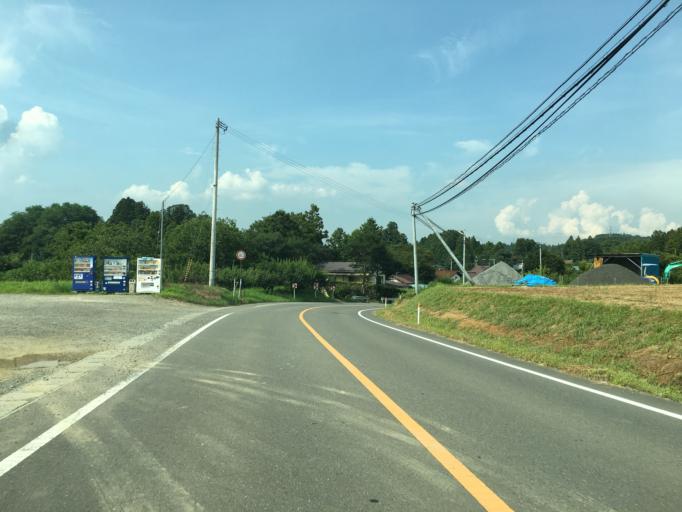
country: JP
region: Fukushima
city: Koriyama
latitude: 37.3493
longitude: 140.4135
